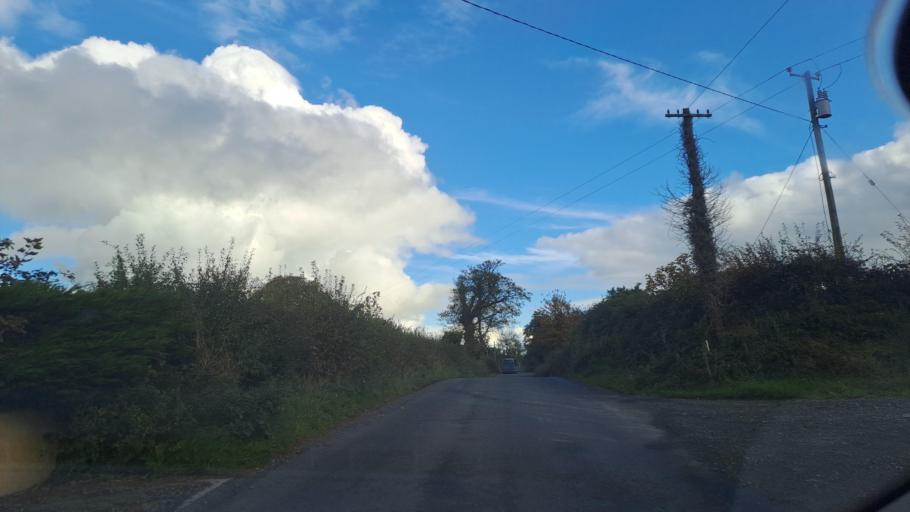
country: IE
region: Ulster
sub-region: An Cabhan
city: Bailieborough
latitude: 53.9959
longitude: -6.9719
